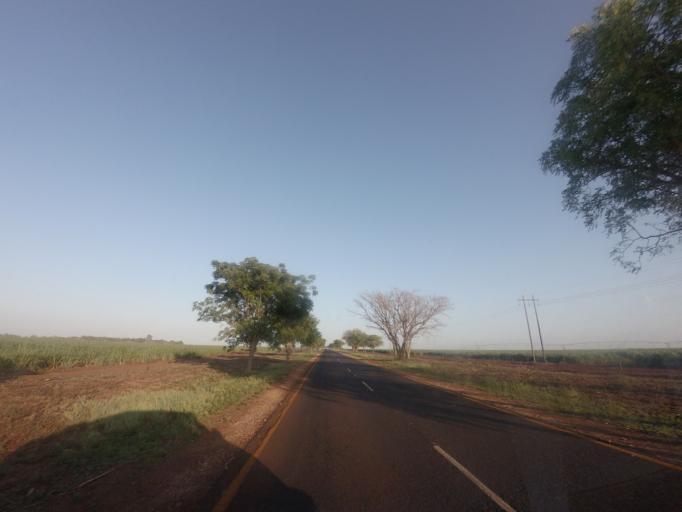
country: ZA
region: Mpumalanga
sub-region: Ehlanzeni District
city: Komatipoort
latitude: -25.4044
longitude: 31.9261
